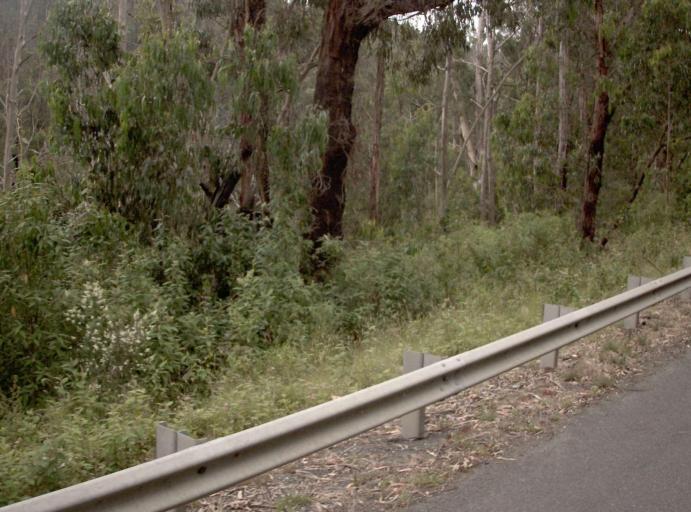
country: AU
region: Victoria
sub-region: Yarra Ranges
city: Yarra Glen
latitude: -37.5420
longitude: 145.4160
